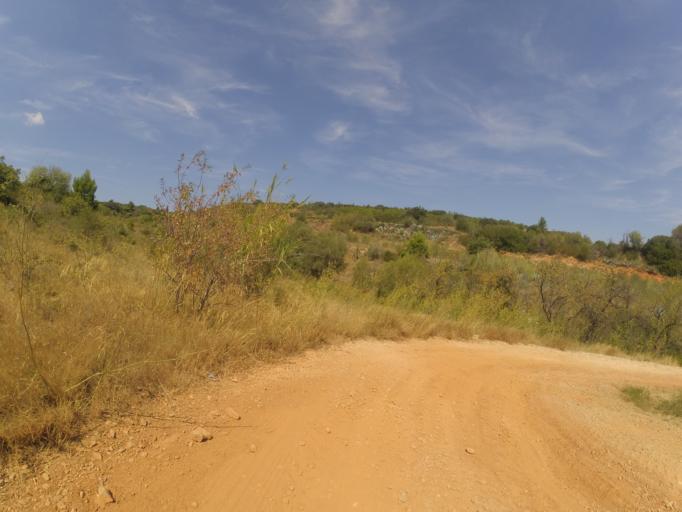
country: FR
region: Languedoc-Roussillon
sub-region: Departement des Pyrenees-Orientales
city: Baixas
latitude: 42.7504
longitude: 2.7996
